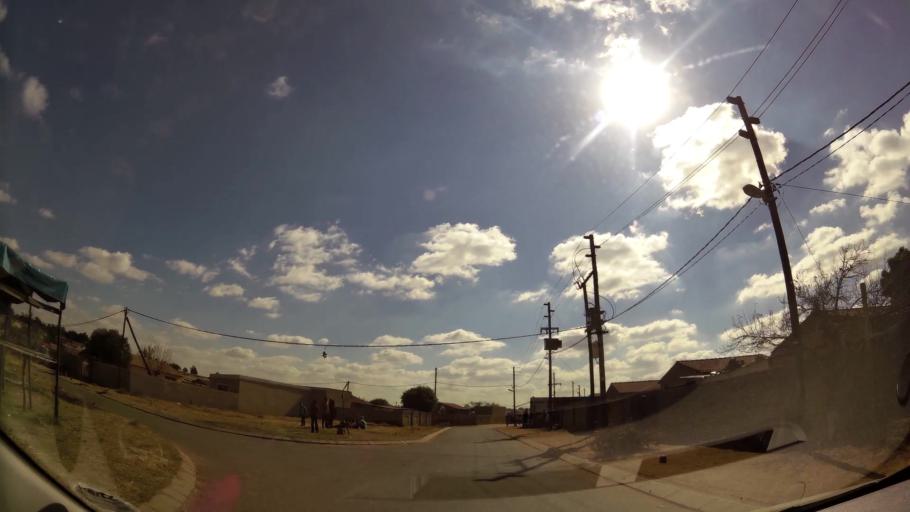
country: ZA
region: Gauteng
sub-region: West Rand District Municipality
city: Krugersdorp
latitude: -26.1457
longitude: 27.7839
